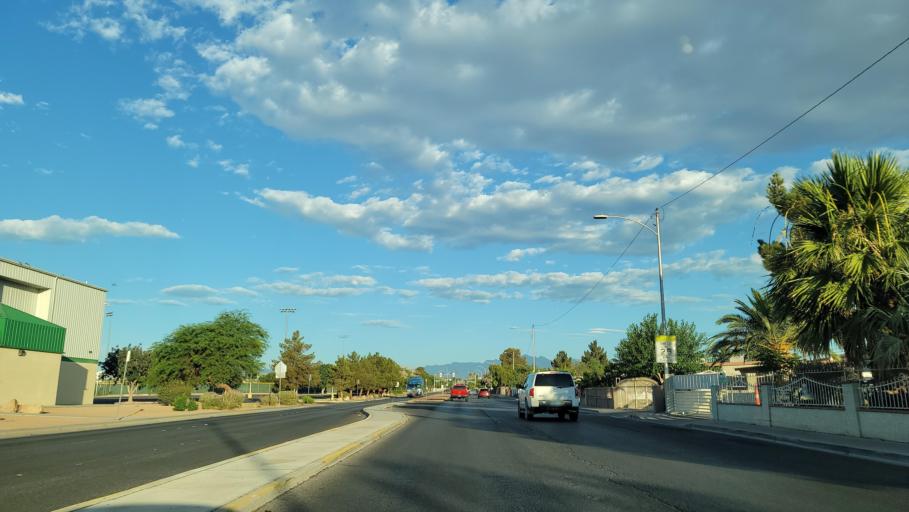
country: US
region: Nevada
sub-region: Clark County
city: North Las Vegas
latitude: 36.1885
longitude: -115.1207
